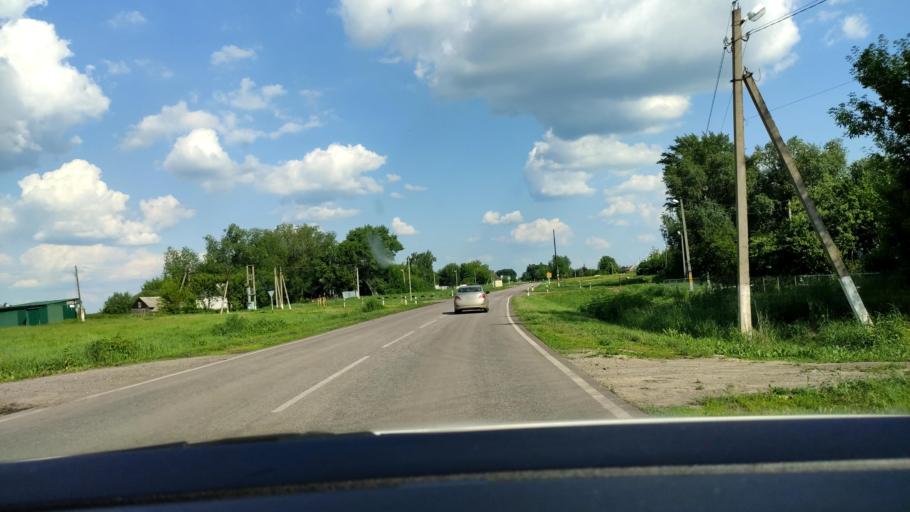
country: RU
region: Voronezj
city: Verkhnyaya Khava
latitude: 51.6727
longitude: 39.9513
